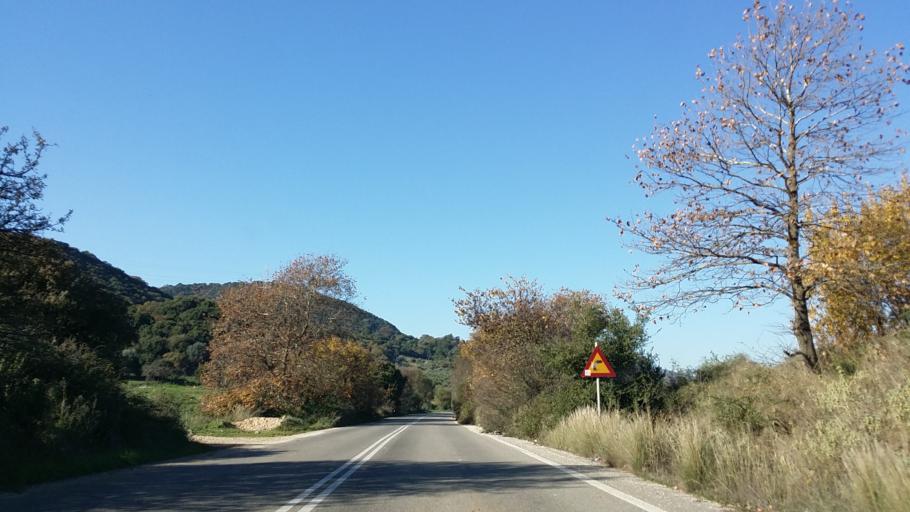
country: GR
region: West Greece
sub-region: Nomos Aitolias kai Akarnanias
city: Monastirakion
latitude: 38.8696
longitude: 21.0524
